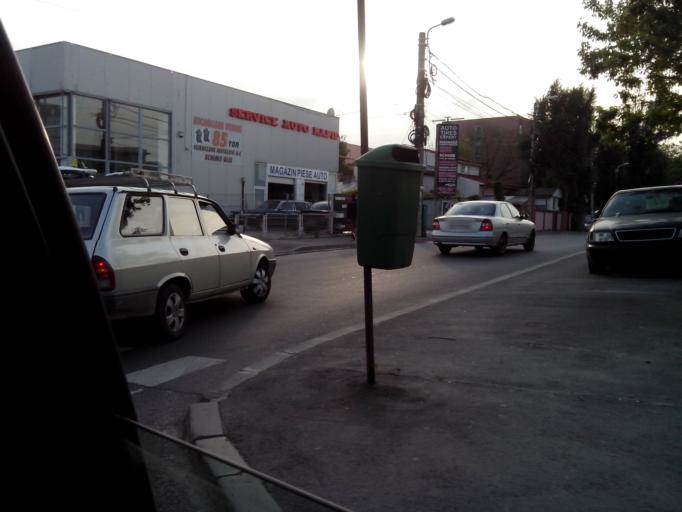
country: RO
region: Ilfov
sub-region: Comuna Chiajna
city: Rosu
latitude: 44.4438
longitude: 26.0363
